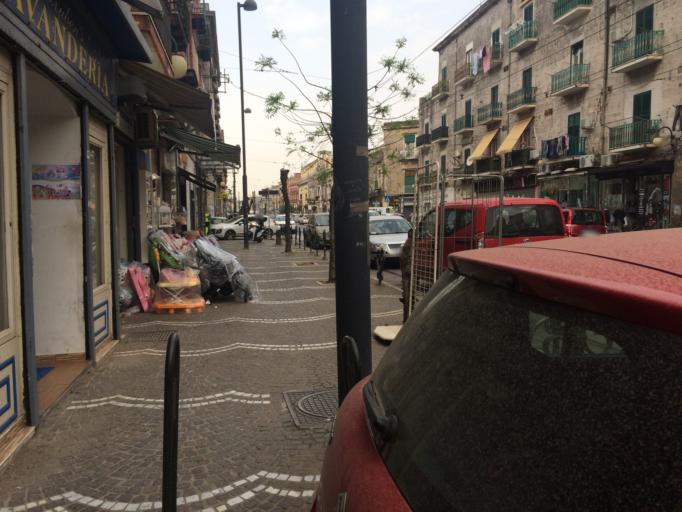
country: IT
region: Campania
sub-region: Provincia di Napoli
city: San Giorgio a Cremano
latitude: 40.8350
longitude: 14.3045
